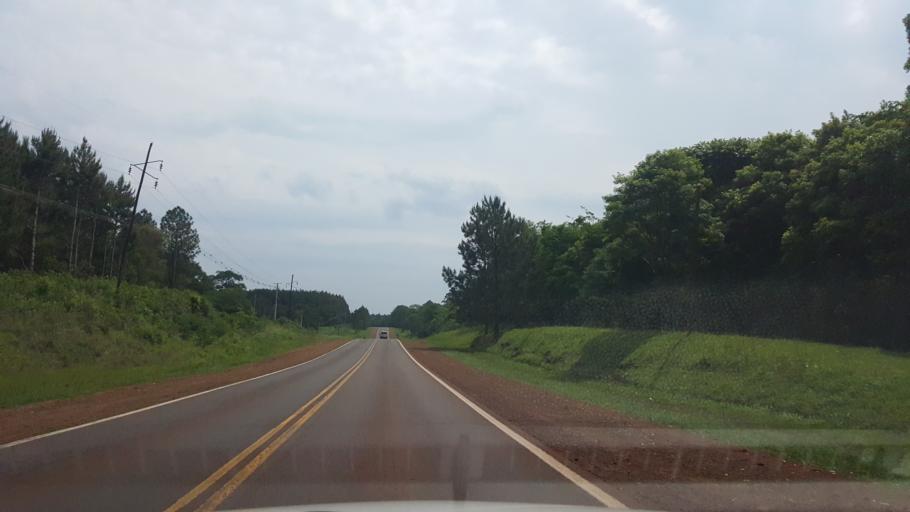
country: AR
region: Misiones
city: Capiovi
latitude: -26.9366
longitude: -55.0694
